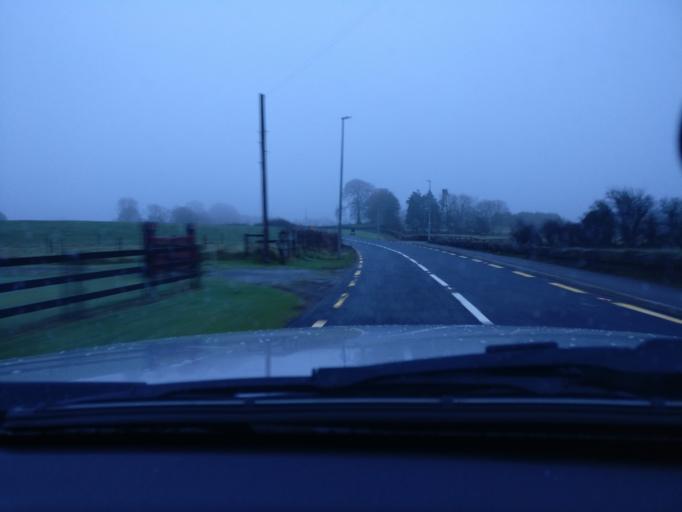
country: IE
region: Leinster
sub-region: An Iarmhi
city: Rathwire
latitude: 53.6127
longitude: -7.0767
